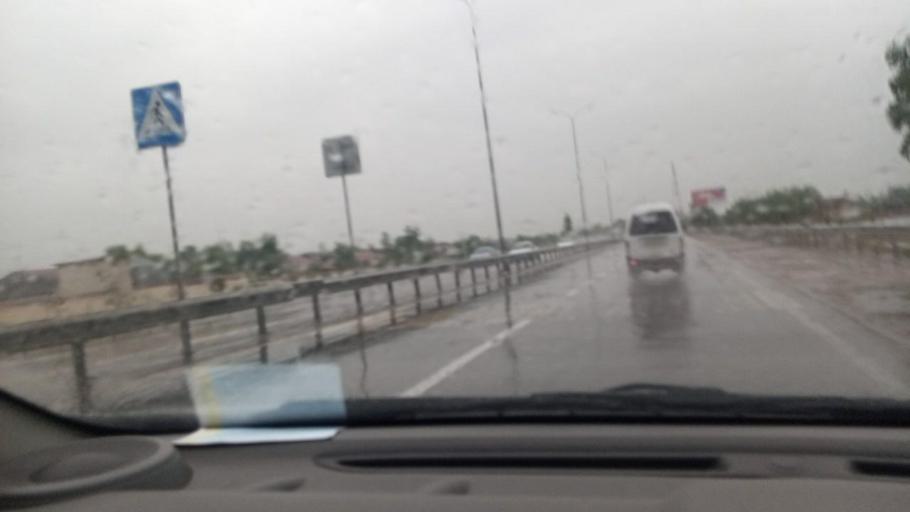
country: UZ
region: Toshkent
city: Tuytepa
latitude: 41.1286
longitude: 69.4369
